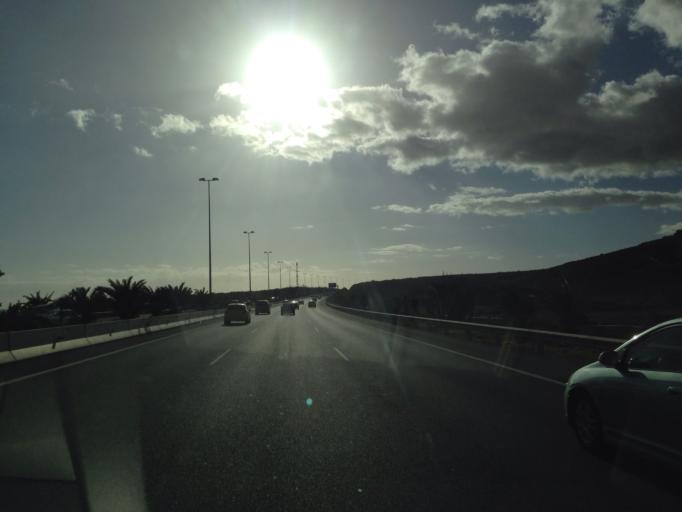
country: ES
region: Canary Islands
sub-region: Provincia de Las Palmas
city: Playa del Ingles
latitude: 27.7932
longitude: -15.4949
